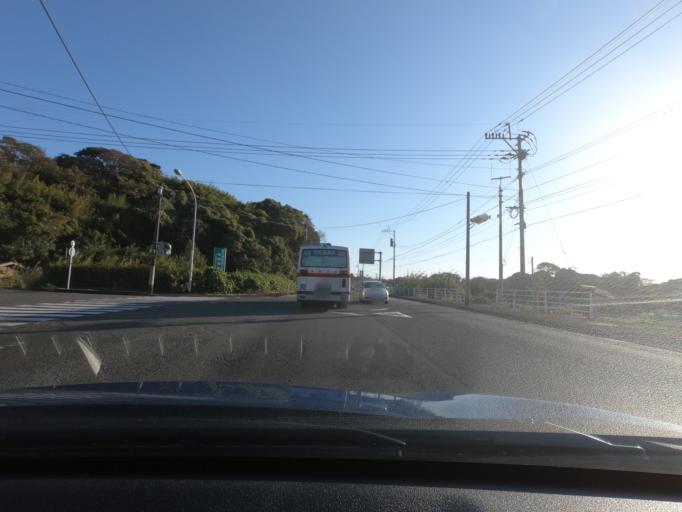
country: JP
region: Kagoshima
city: Akune
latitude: 31.9840
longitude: 130.2038
